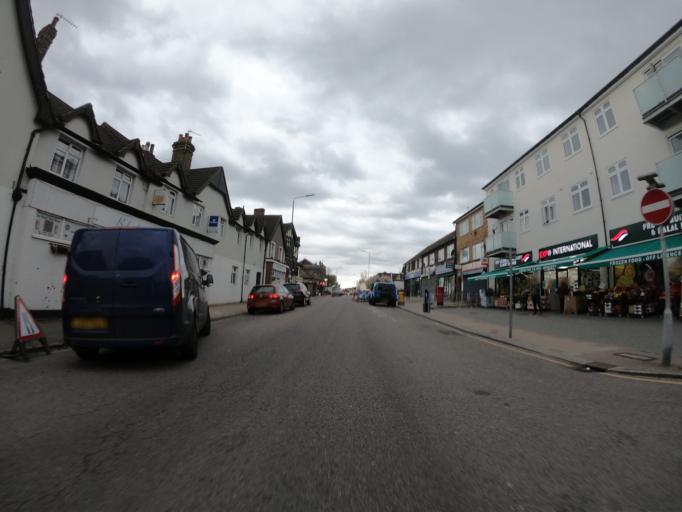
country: GB
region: England
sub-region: Greater London
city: Belvedere
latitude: 51.4828
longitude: 0.1466
